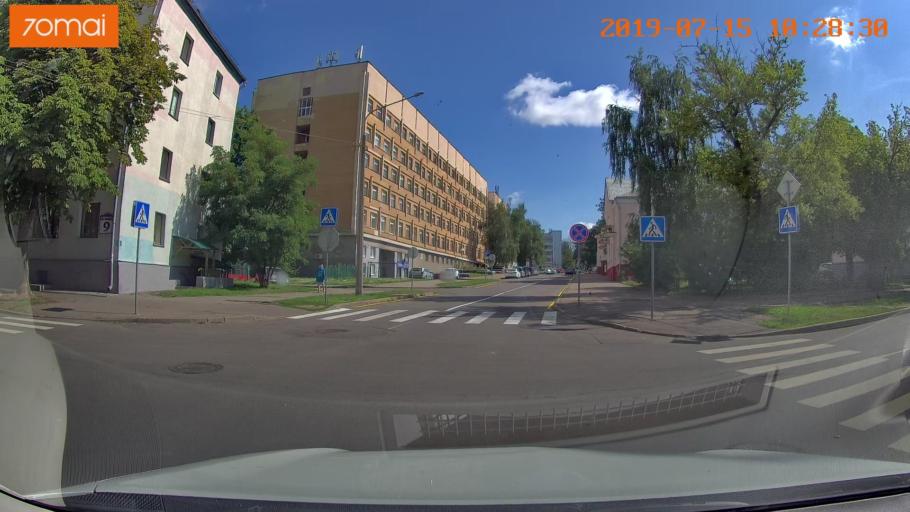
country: BY
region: Minsk
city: Minsk
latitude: 53.9101
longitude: 27.5844
